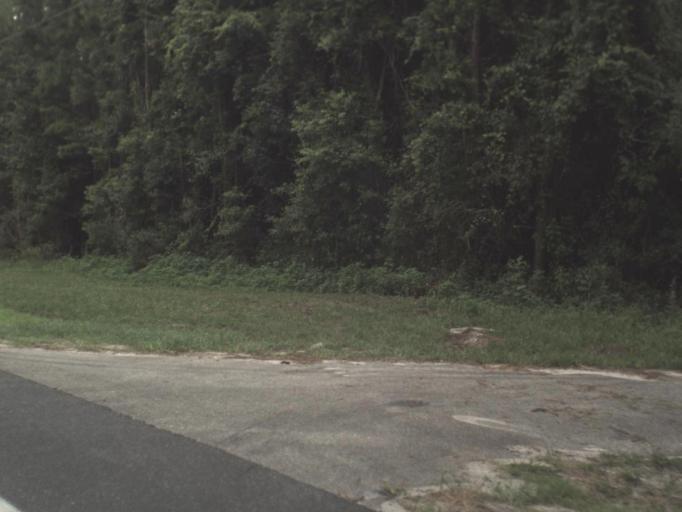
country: US
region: Florida
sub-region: Alachua County
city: Archer
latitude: 29.5411
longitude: -82.5206
